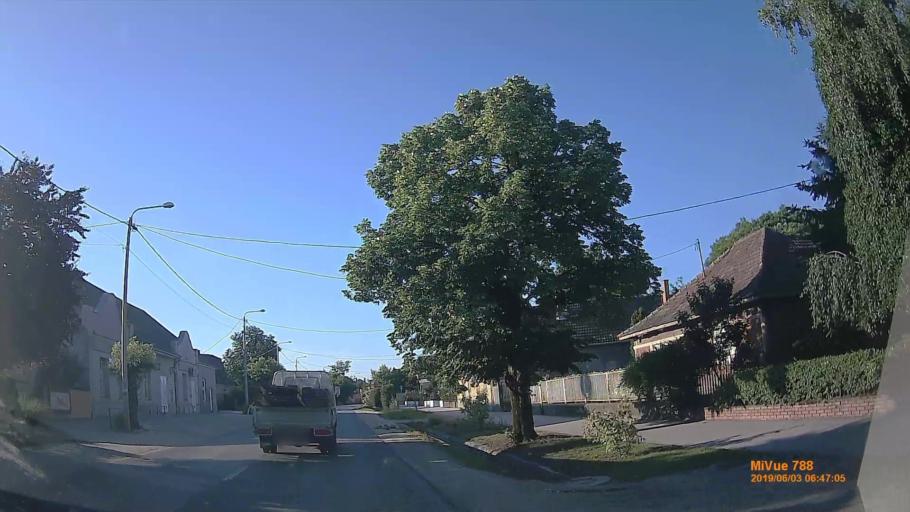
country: HU
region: Pest
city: Bugyi
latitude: 47.2273
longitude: 19.1477
